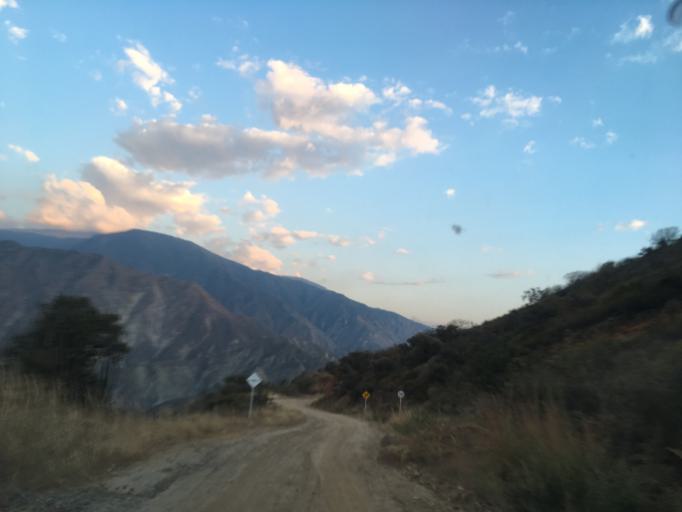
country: CO
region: Santander
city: Aratoca
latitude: 6.8013
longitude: -72.9927
